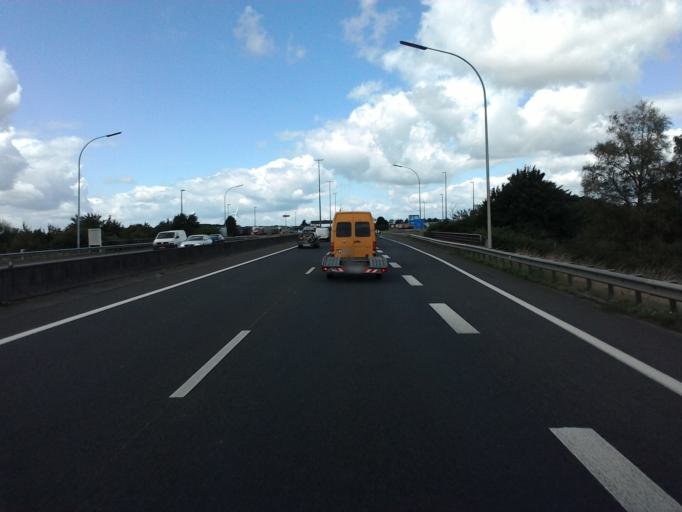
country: LU
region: Luxembourg
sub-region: Canton de Capellen
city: Steinfort
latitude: 49.6383
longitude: 5.9081
